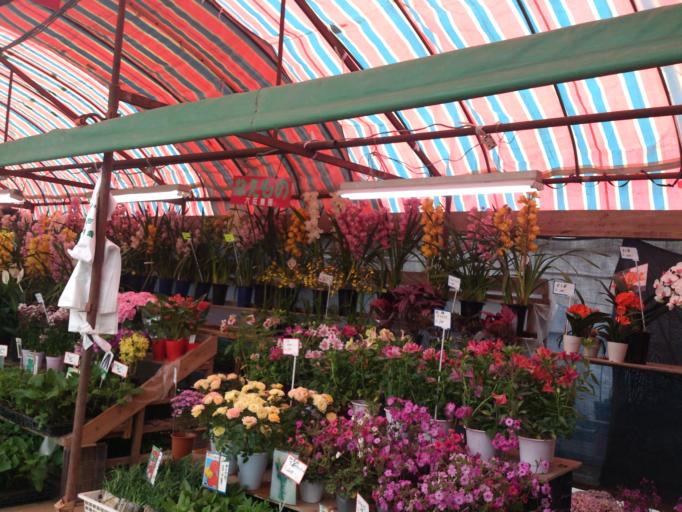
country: JP
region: Kagoshima
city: Kagoshima-shi
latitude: 31.5878
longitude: 130.5459
